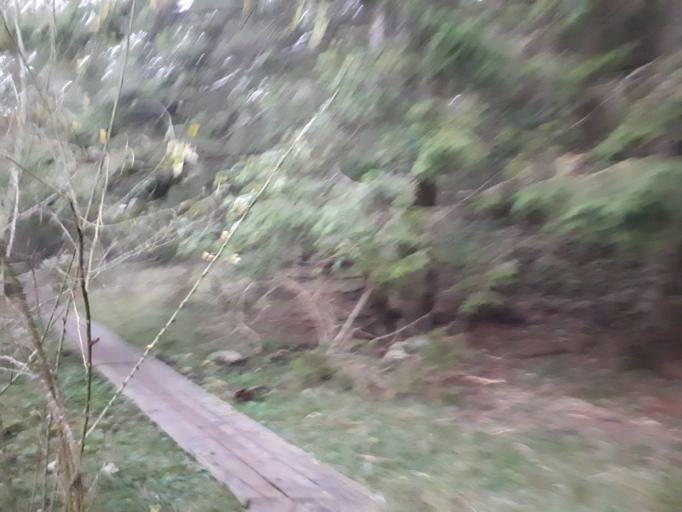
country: SE
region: Gotland
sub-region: Gotland
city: Visby
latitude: 57.6856
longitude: 18.3475
